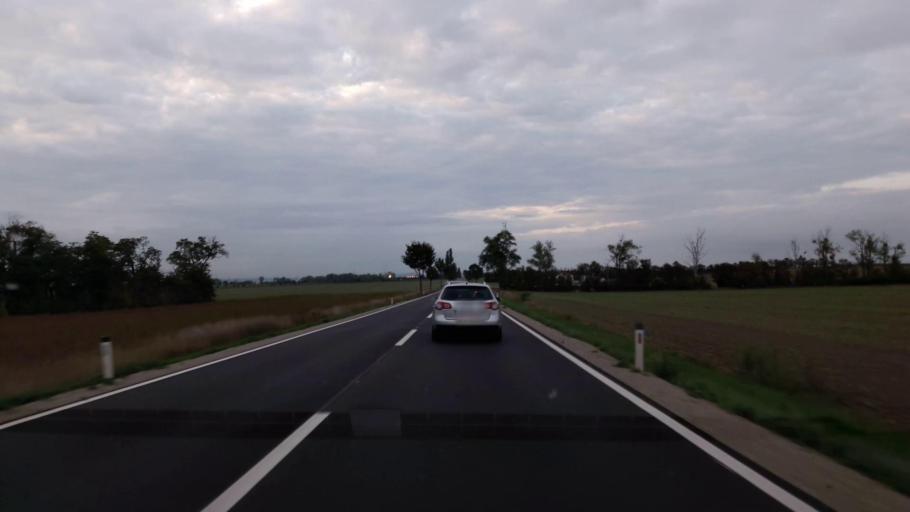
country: AT
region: Lower Austria
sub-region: Politischer Bezirk Wien-Umgebung
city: Rauchenwarth
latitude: 48.1207
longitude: 16.5119
